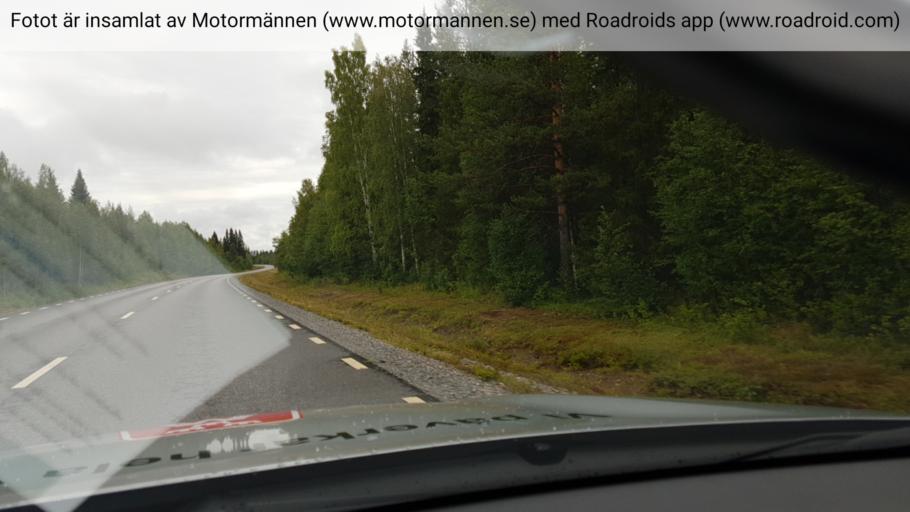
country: SE
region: Norrbotten
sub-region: Alvsbyns Kommun
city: AElvsbyn
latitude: 66.3227
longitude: 20.7772
